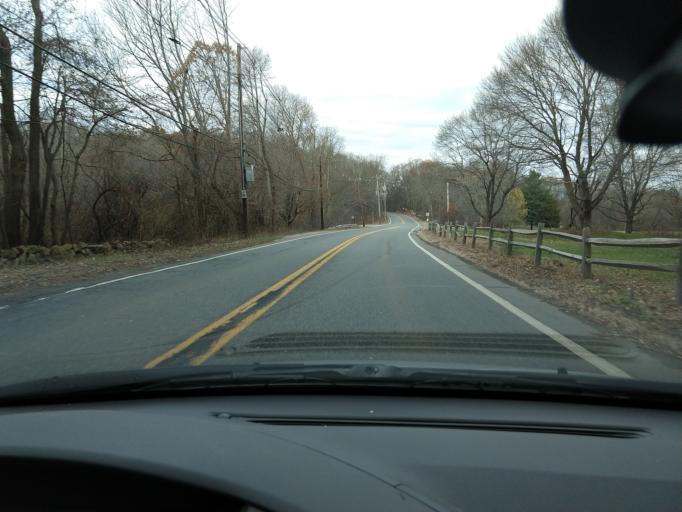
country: US
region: Massachusetts
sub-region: Middlesex County
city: Lincoln
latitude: 42.4493
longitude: -71.2882
